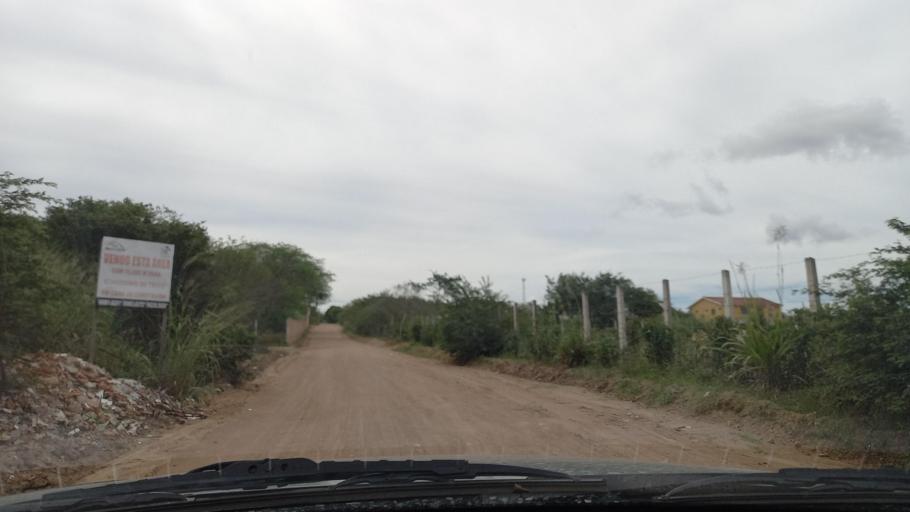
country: BR
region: Pernambuco
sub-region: Gravata
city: Gravata
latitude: -8.1978
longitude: -35.5908
